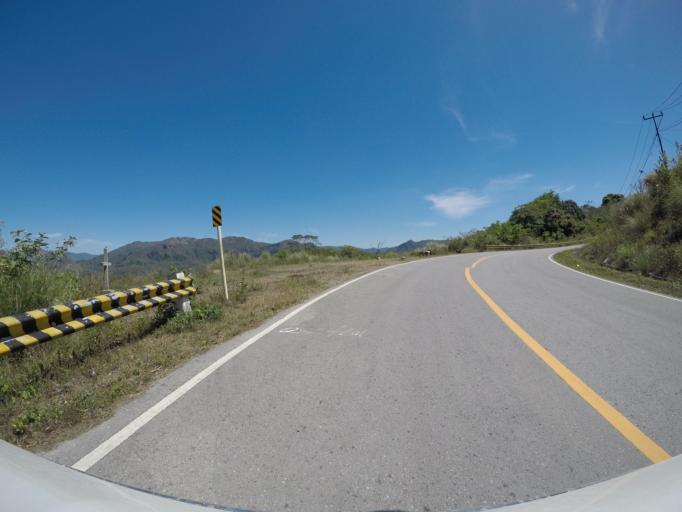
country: TL
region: Manatuto
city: Manatuto
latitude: -8.8035
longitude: 125.9685
